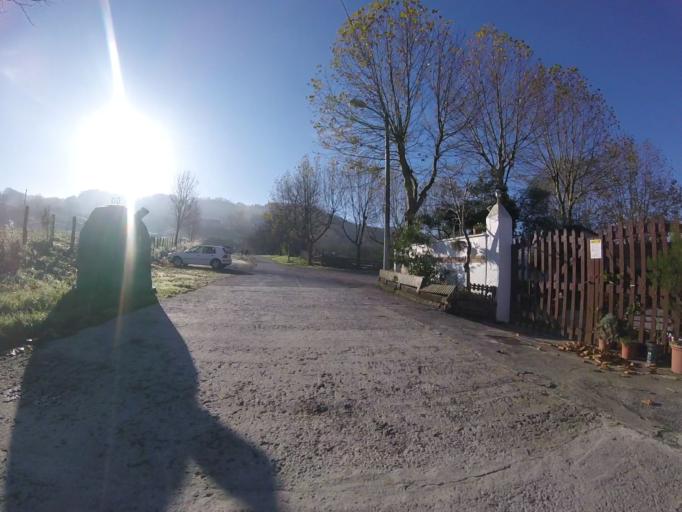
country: ES
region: Basque Country
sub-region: Provincia de Guipuzcoa
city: Lasarte
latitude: 43.2692
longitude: -2.0351
